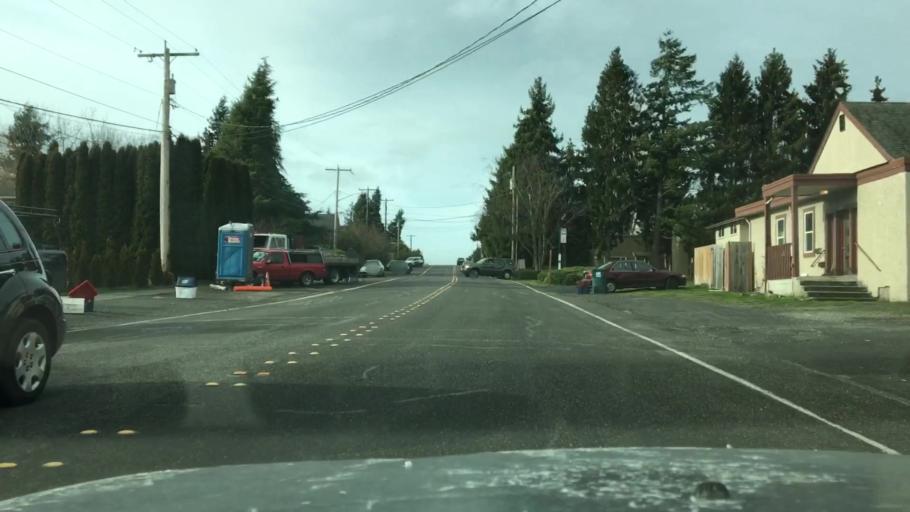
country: US
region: Washington
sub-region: Whatcom County
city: Bellingham
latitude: 48.7202
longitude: -122.4906
